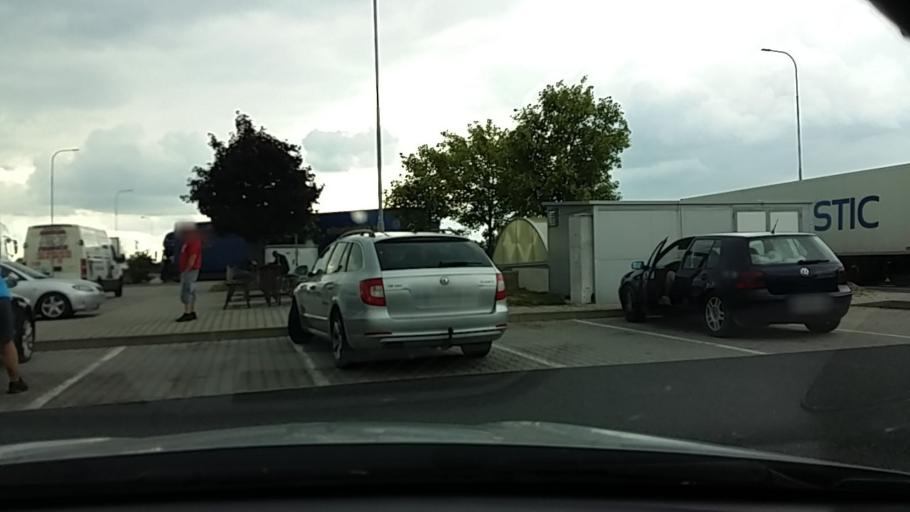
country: CZ
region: Plzensky
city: Bor
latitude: 49.7460
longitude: 12.8431
